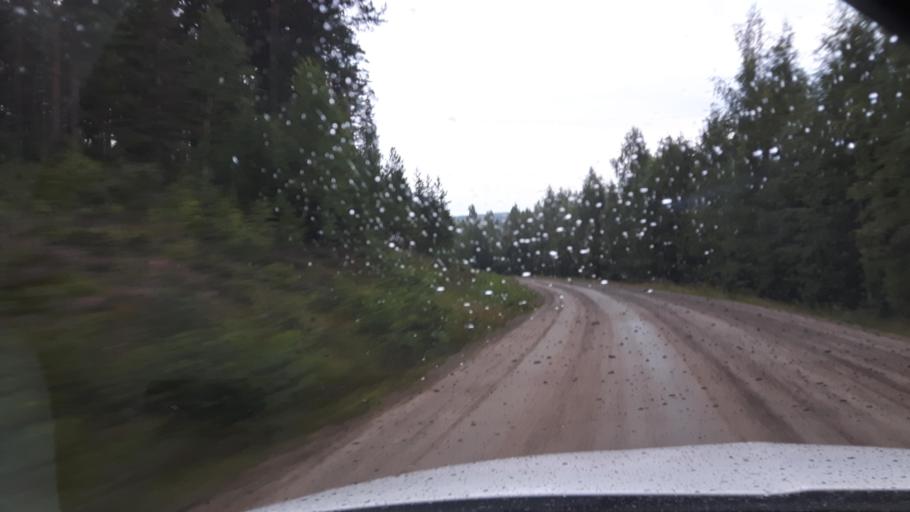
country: SE
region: Gaevleborg
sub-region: Ljusdals Kommun
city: Farila
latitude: 62.0091
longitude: 15.8361
